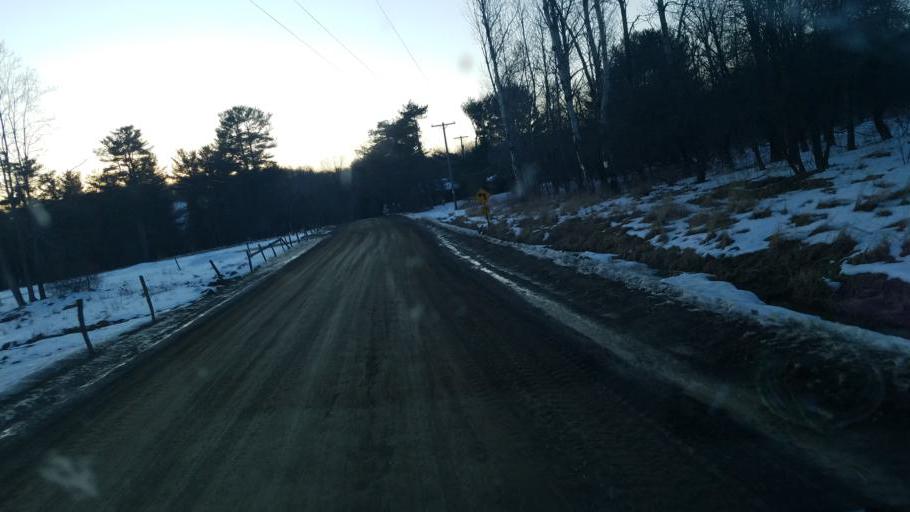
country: US
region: Pennsylvania
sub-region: Tioga County
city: Westfield
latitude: 42.0129
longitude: -77.6811
